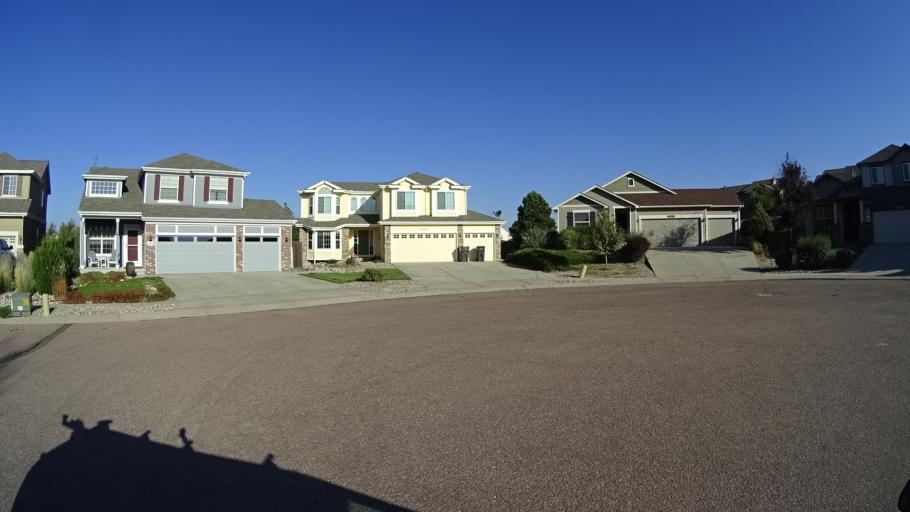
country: US
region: Colorado
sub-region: El Paso County
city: Cimarron Hills
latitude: 38.8946
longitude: -104.7011
